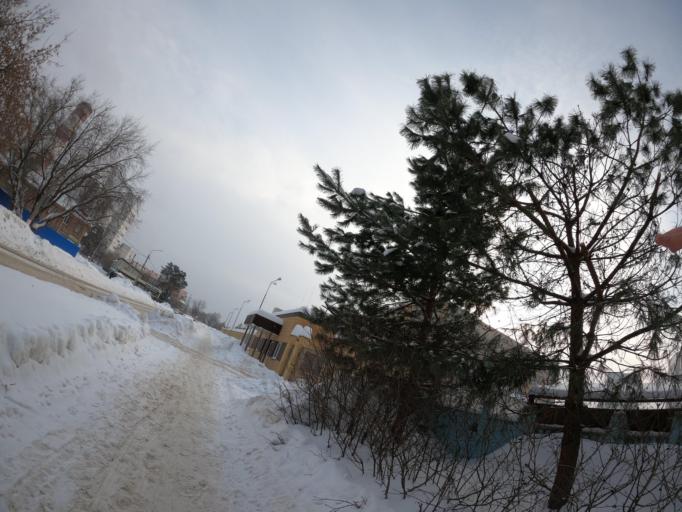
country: RU
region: Moskovskaya
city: Elektrogorsk
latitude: 55.8873
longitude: 38.7759
